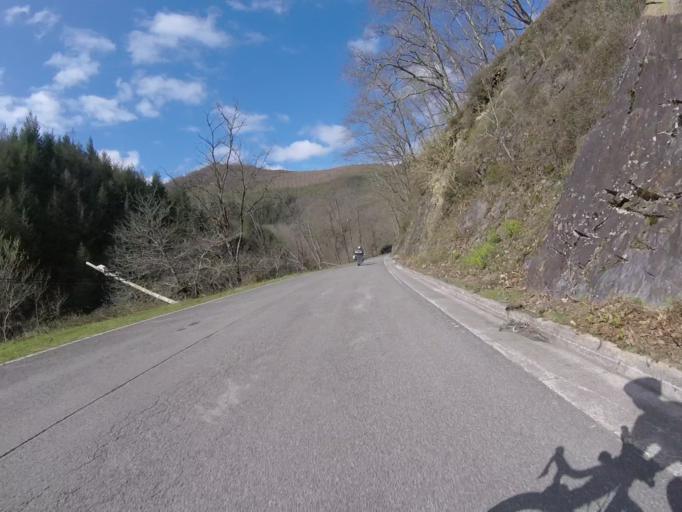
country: ES
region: Navarre
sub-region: Provincia de Navarra
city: Goizueta
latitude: 43.1551
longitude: -1.8487
